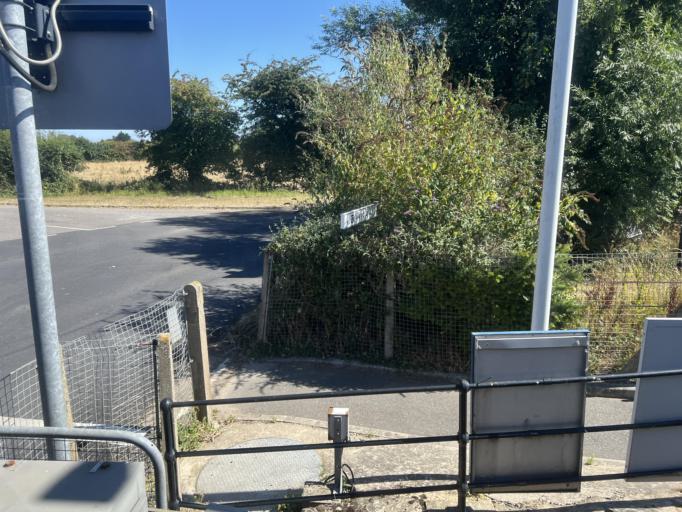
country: GB
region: England
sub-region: Lincolnshire
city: Wainfleet All Saints
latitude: 53.1232
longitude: 0.1993
